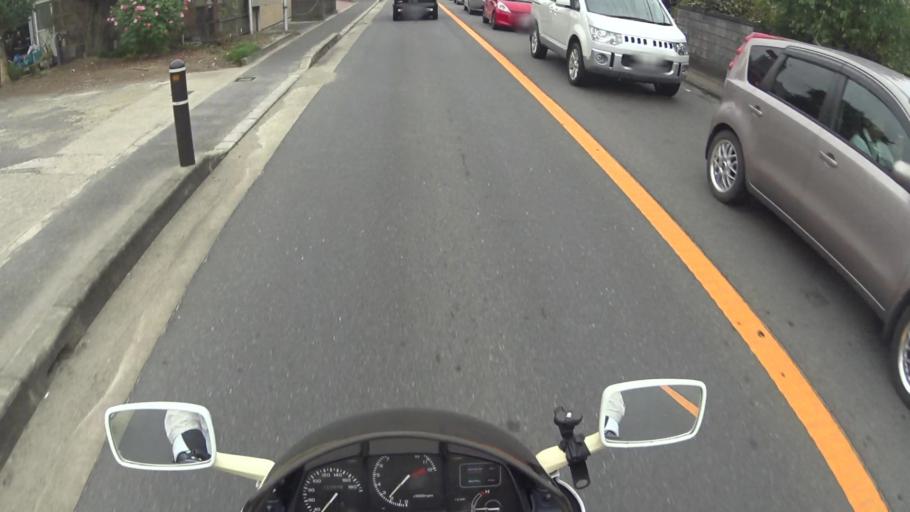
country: JP
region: Kyoto
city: Uji
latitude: 34.8641
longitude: 135.7770
